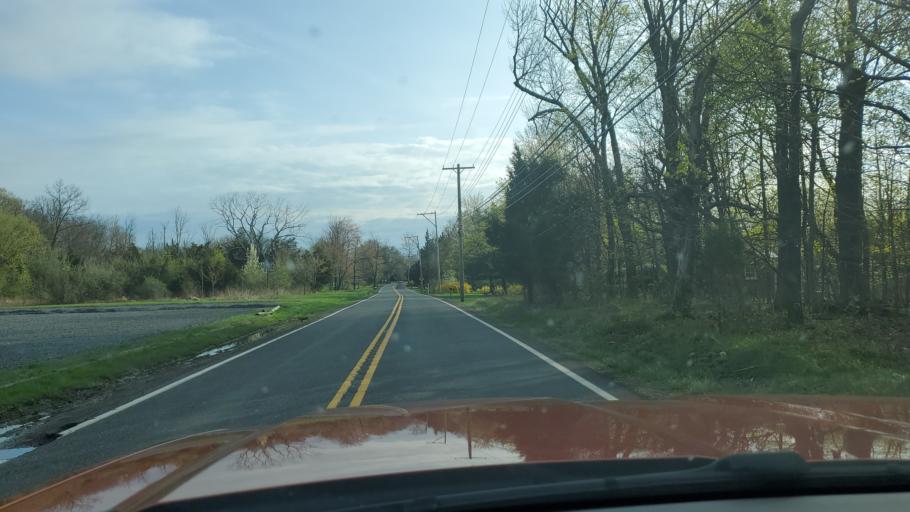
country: US
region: Pennsylvania
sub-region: Montgomery County
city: Woxall
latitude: 40.3208
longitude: -75.4253
